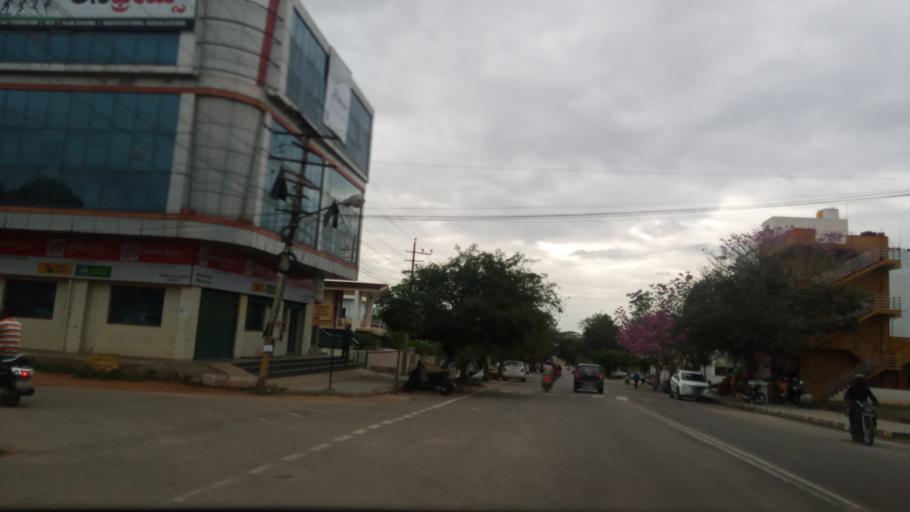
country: IN
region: Karnataka
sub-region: Mysore
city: Mysore
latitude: 12.2953
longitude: 76.6104
